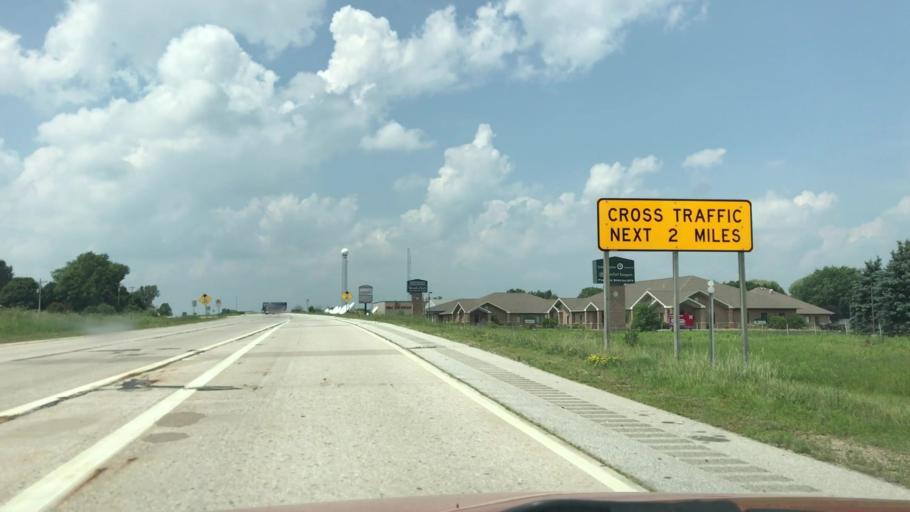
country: US
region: Wisconsin
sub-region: Brown County
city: Ashwaubenon
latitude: 44.4888
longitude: -88.0883
